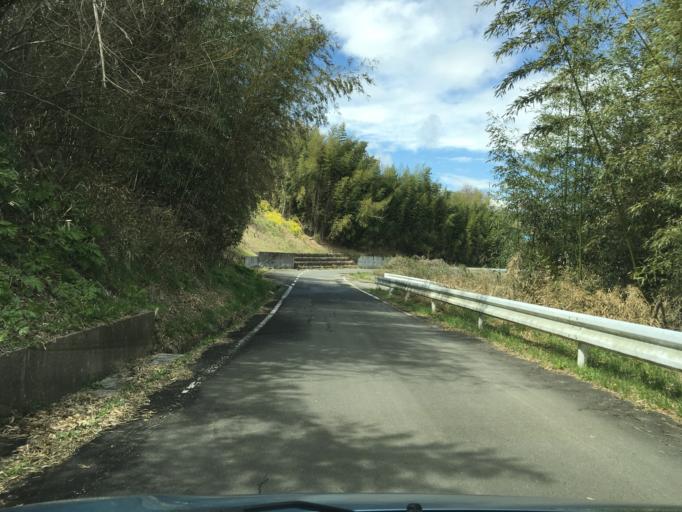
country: JP
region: Miyagi
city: Wakuya
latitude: 38.7072
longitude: 141.1399
